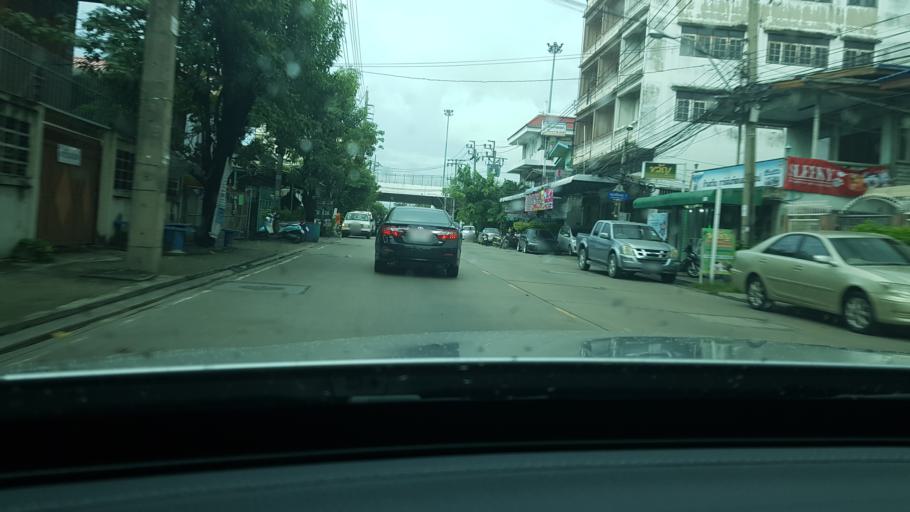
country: TH
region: Samut Prakan
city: Phra Pradaeng
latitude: 13.6656
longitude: 100.5267
